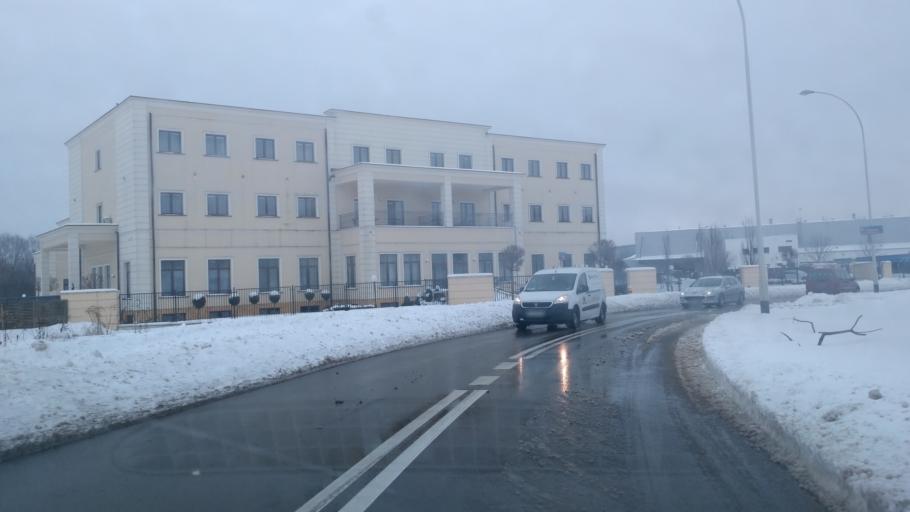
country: PL
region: Subcarpathian Voivodeship
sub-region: Rzeszow
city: Rzeszow
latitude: 50.0585
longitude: 22.0130
